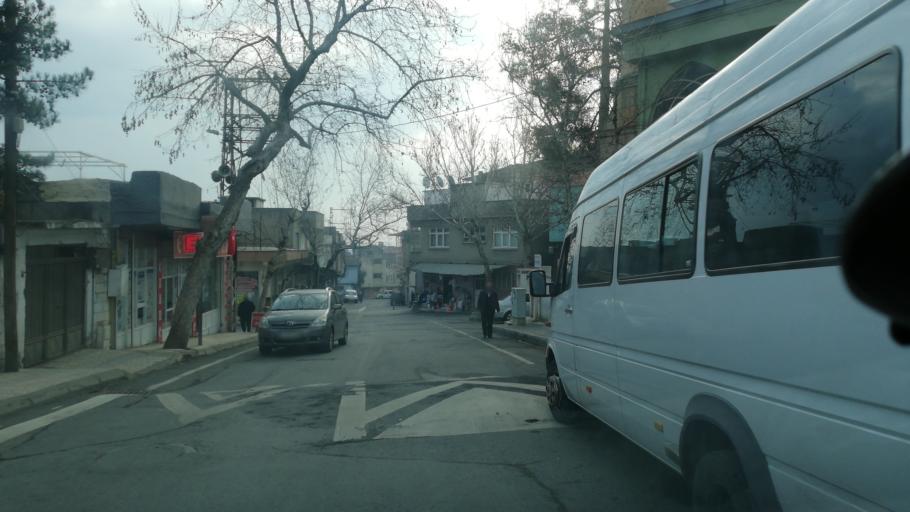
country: TR
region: Kahramanmaras
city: Kahramanmaras
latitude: 37.5896
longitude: 36.9103
